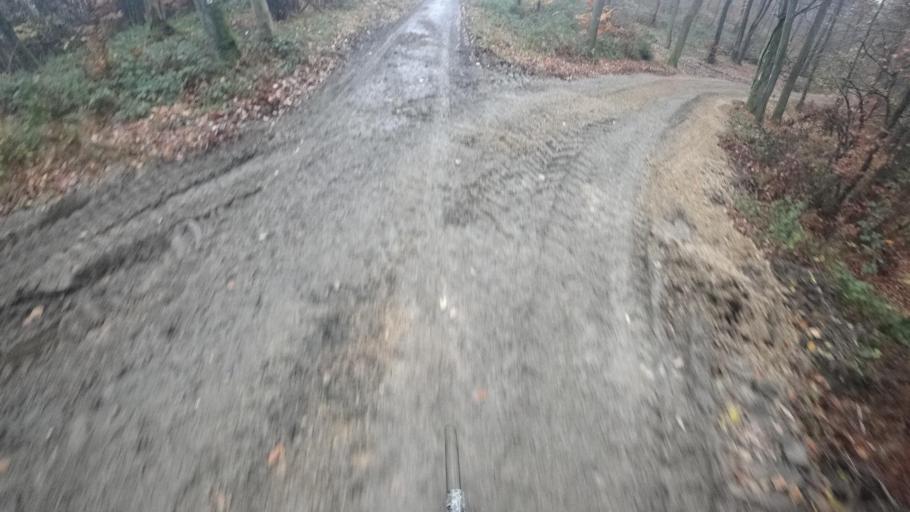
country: DE
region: Rheinland-Pfalz
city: Kesseling
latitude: 50.4976
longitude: 7.0211
